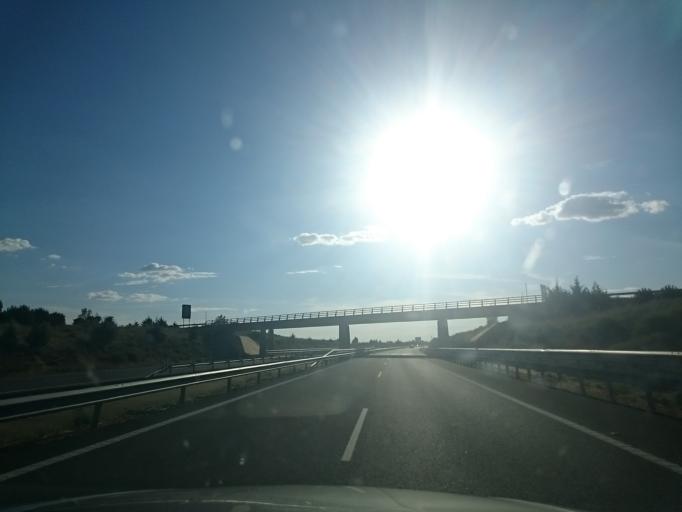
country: ES
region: Castille and Leon
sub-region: Provincia de Burgos
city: Melgar de Fernamental
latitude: 42.4018
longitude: -4.2137
